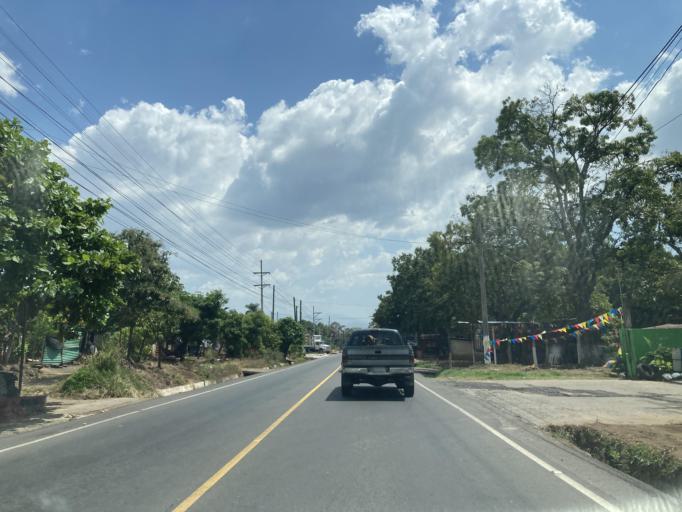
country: GT
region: Santa Rosa
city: Guazacapan
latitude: 14.0675
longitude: -90.4118
